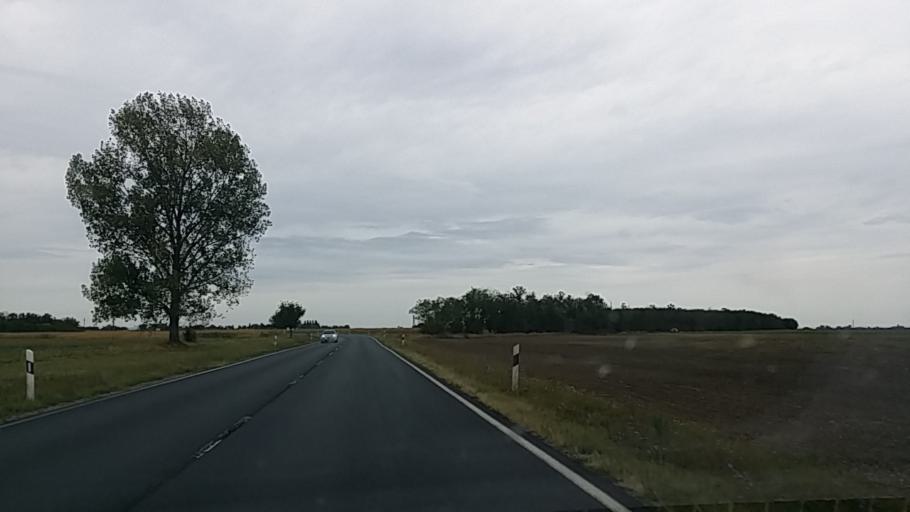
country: HU
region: Gyor-Moson-Sopron
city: Fertoszentmiklos
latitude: 47.5955
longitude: 16.9325
